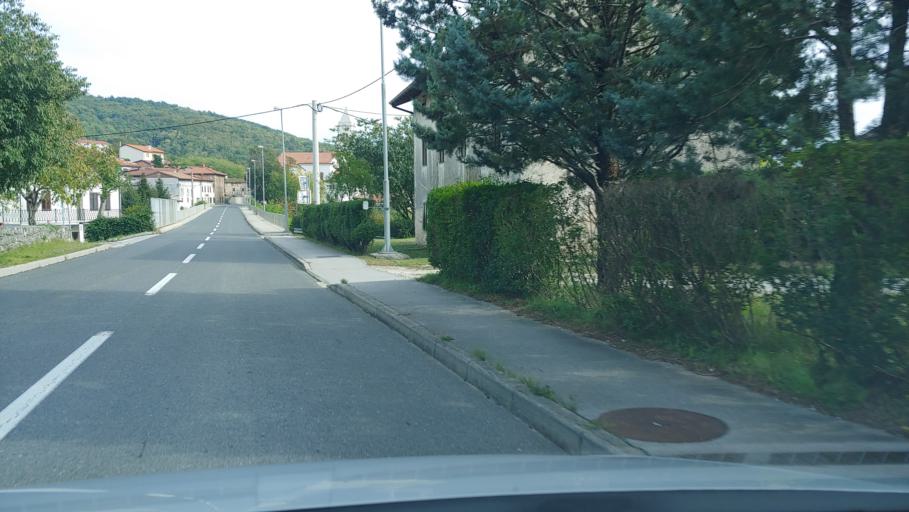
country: SI
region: Nova Gorica
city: Sempas
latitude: 45.9089
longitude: 13.7737
